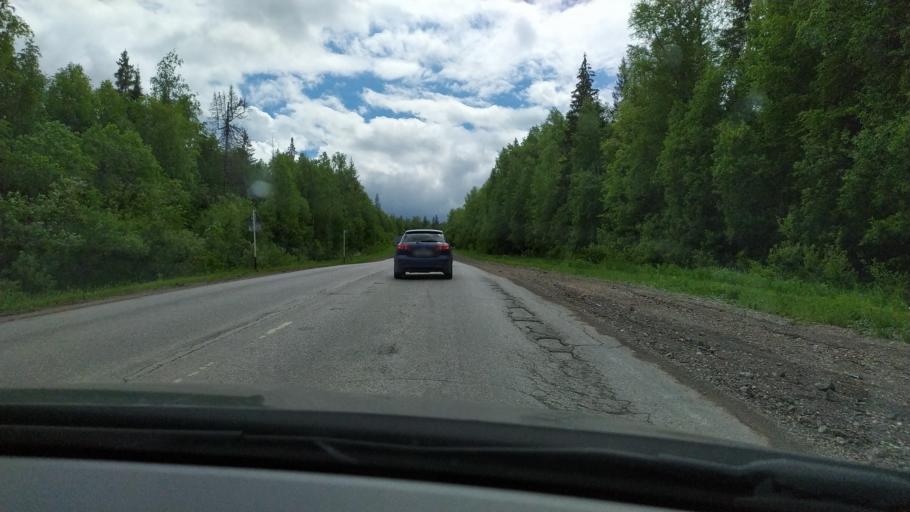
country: RU
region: Perm
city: Gremyachinsk
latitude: 58.4363
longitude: 57.8842
